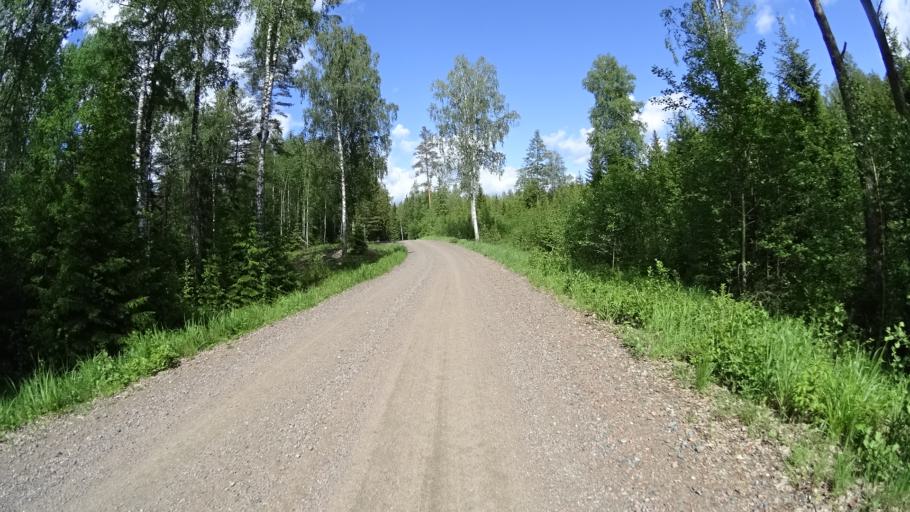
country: FI
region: Uusimaa
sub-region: Raaseporin
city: Karis
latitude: 60.1353
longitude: 23.6220
